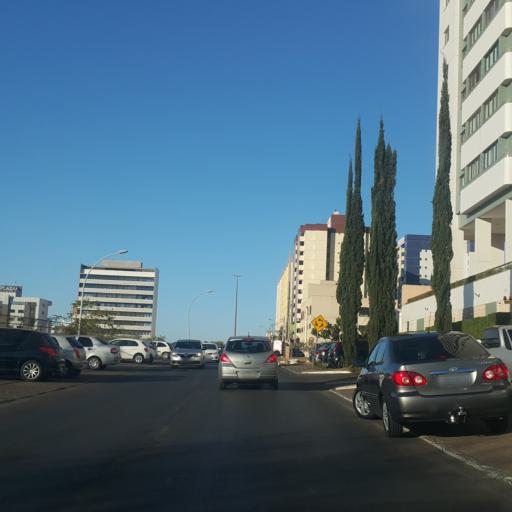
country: BR
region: Federal District
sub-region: Brasilia
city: Brasilia
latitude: -15.8331
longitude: -48.0192
